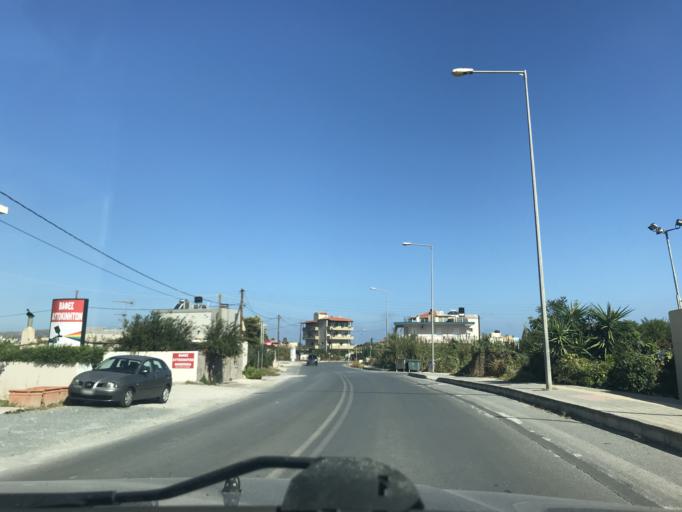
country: GR
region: Crete
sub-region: Nomos Irakleiou
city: Gazi
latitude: 35.3302
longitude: 25.0643
